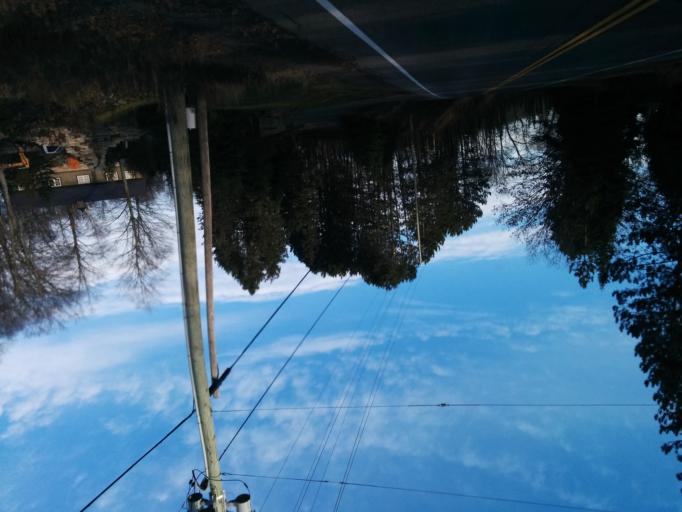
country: CA
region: Ontario
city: Bancroft
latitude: 45.0243
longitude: -78.3819
